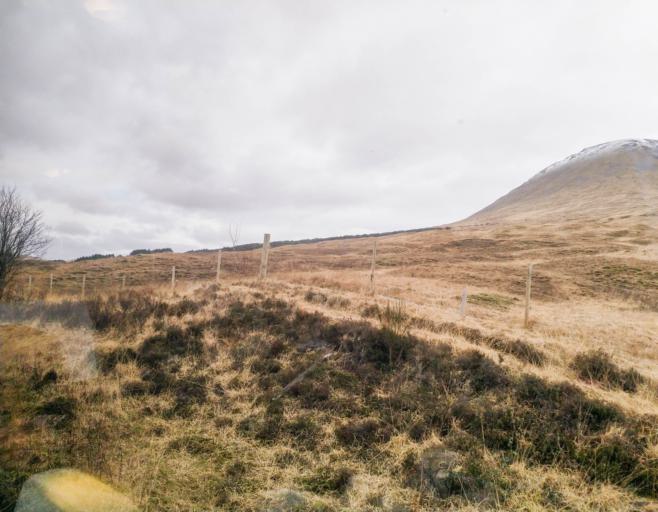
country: GB
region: Scotland
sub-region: Highland
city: Spean Bridge
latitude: 56.5136
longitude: -4.7622
